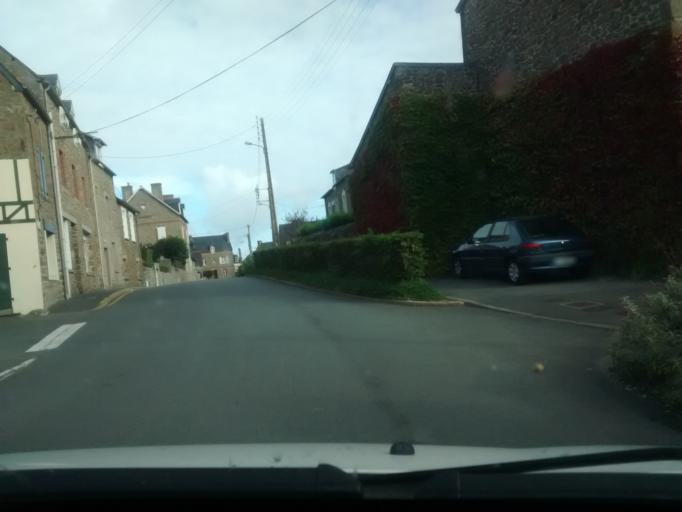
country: FR
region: Brittany
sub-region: Departement d'Ille-et-Vilaine
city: Saint-Lunaire
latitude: 48.6321
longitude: -2.1067
